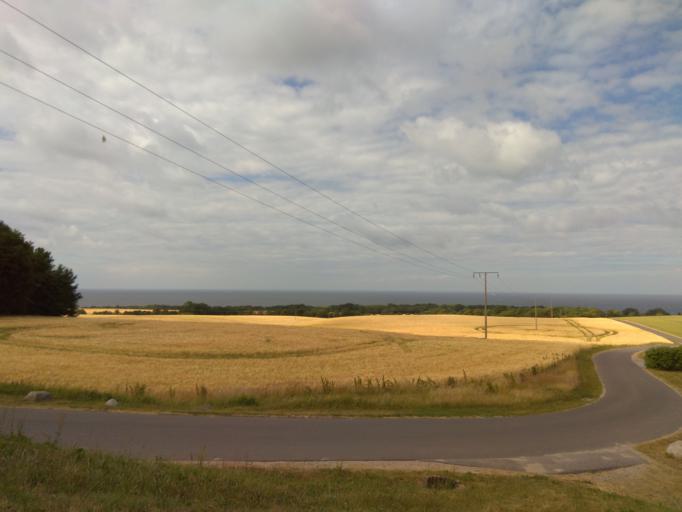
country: DE
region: Mecklenburg-Vorpommern
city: Sagard
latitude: 54.5720
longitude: 13.6017
